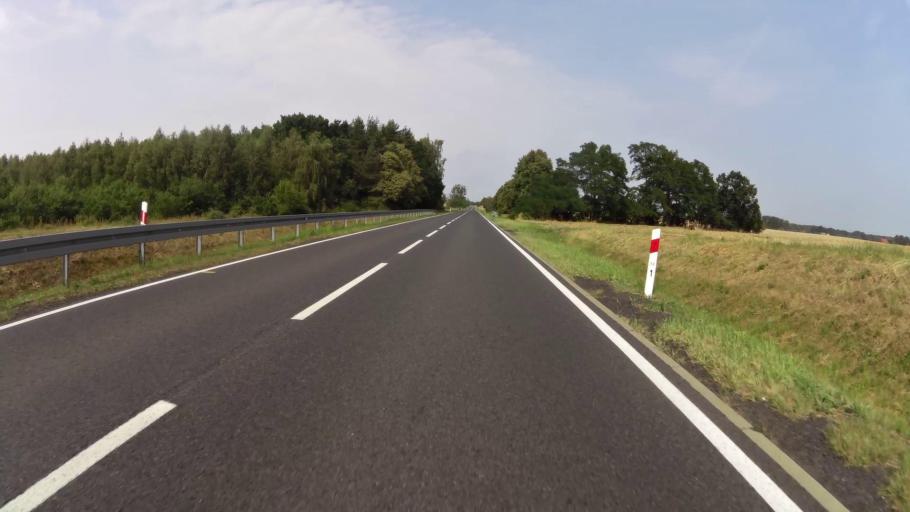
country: PL
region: West Pomeranian Voivodeship
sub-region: Powiat gryfinski
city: Mieszkowice
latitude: 52.8358
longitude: 14.4938
